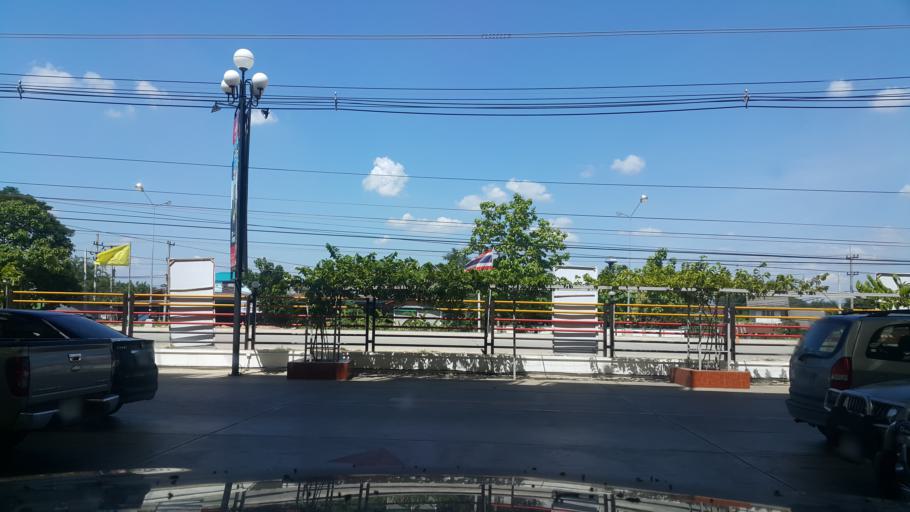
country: TH
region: Chiang Mai
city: Saraphi
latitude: 18.6660
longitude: 99.0509
